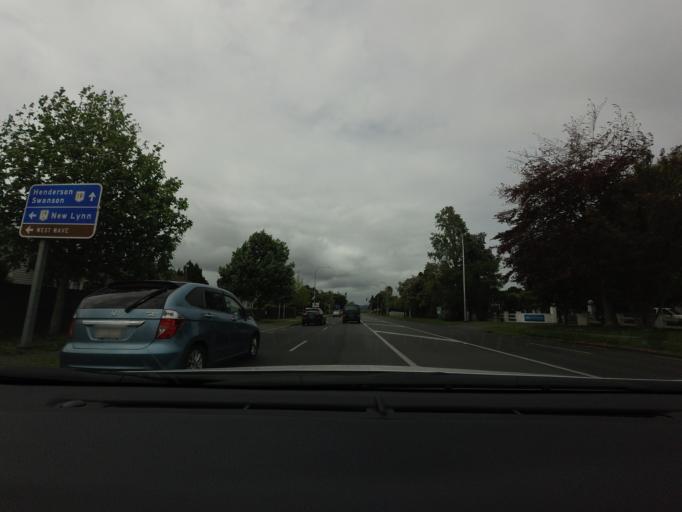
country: NZ
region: Auckland
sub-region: Auckland
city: Rosebank
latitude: -36.8725
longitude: 174.6280
